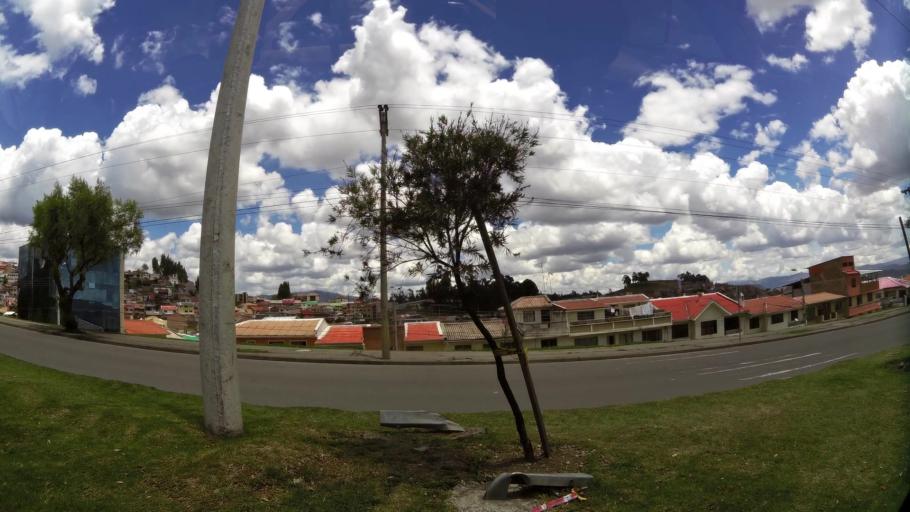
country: EC
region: Azuay
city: Cuenca
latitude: -2.8856
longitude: -78.9991
